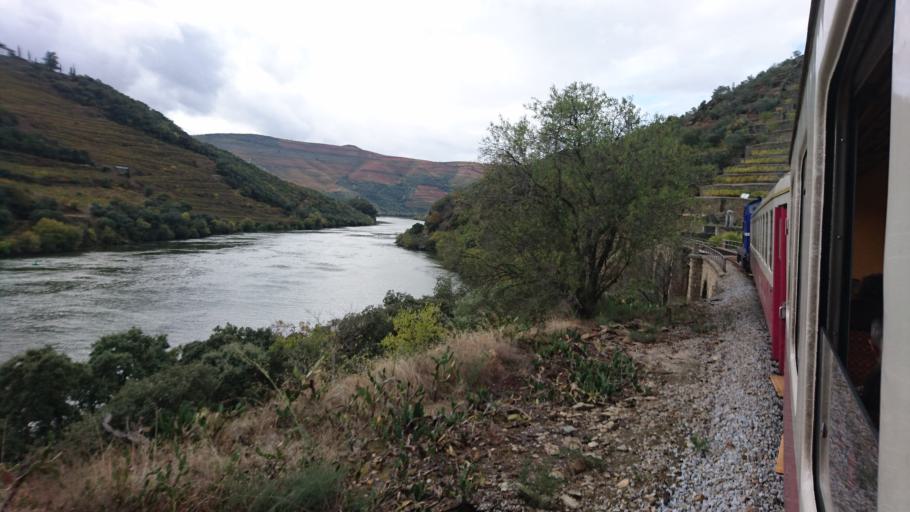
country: PT
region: Vila Real
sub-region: Sabrosa
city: Sabrosa
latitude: 41.1981
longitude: -7.5091
